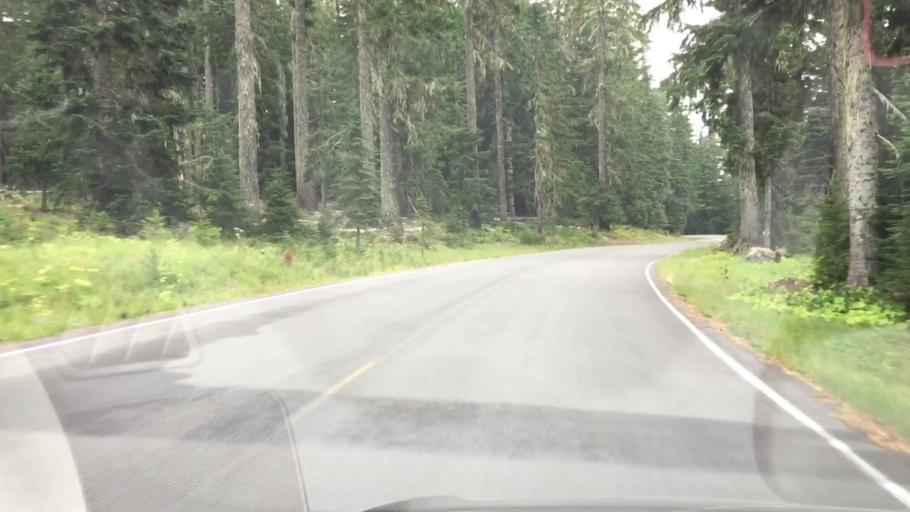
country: US
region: Washington
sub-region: Klickitat County
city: White Salmon
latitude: 46.1857
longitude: -121.6423
